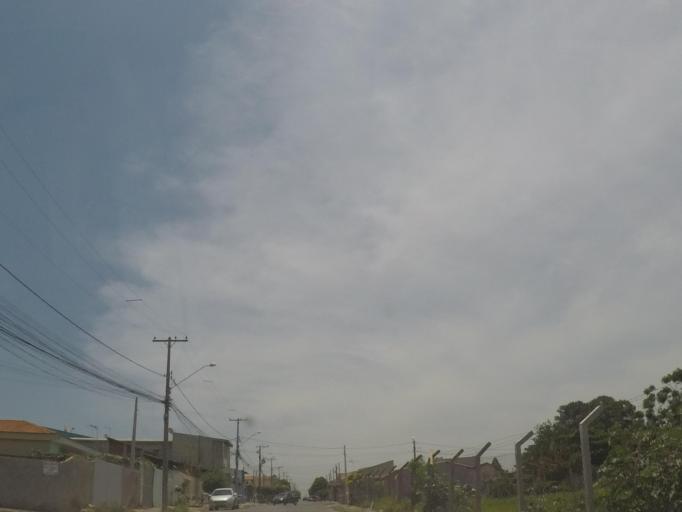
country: BR
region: Sao Paulo
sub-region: Hortolandia
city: Hortolandia
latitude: -22.8514
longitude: -47.1849
